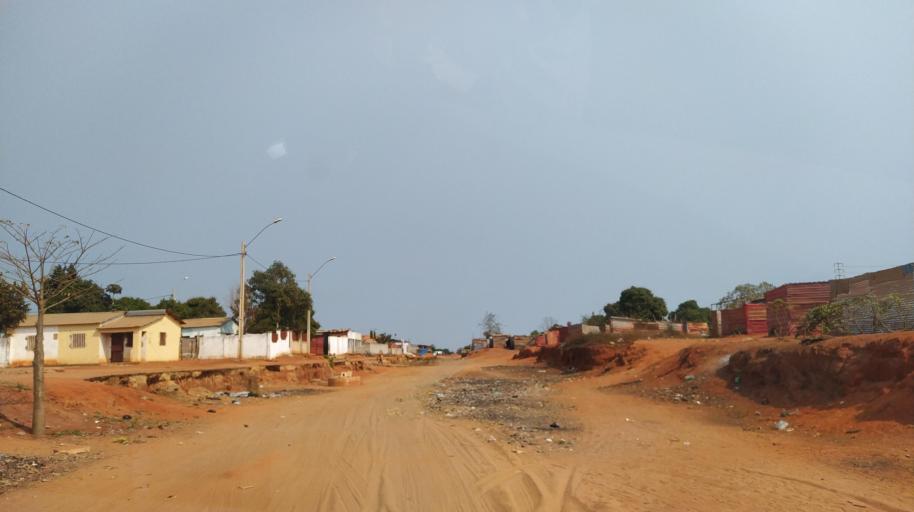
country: AO
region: Luanda
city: Luanda
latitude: -9.0675
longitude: 13.4172
